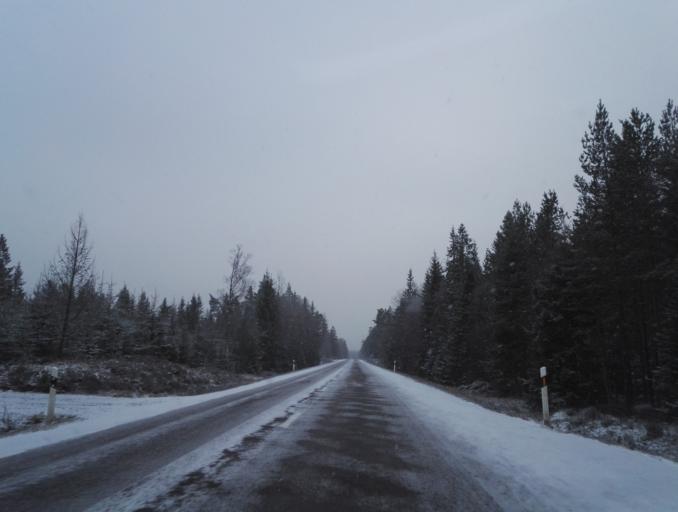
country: SE
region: Kronoberg
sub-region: Uppvidinge Kommun
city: Lenhovda
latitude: 56.8915
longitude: 15.3720
